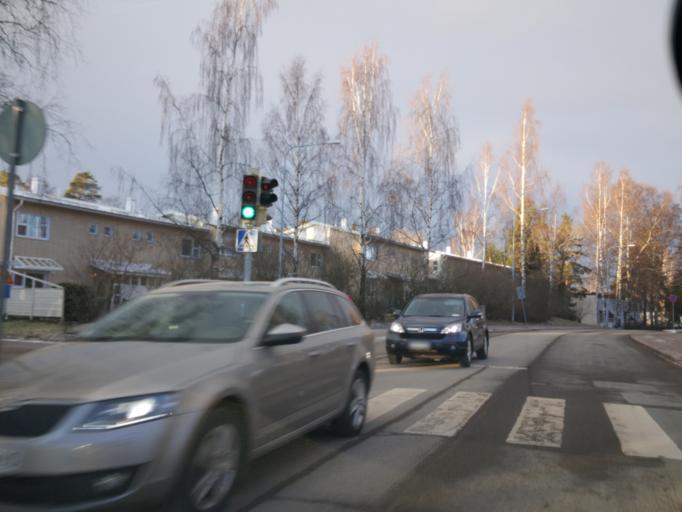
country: FI
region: Uusimaa
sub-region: Helsinki
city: Vantaa
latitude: 60.2494
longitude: 24.9886
